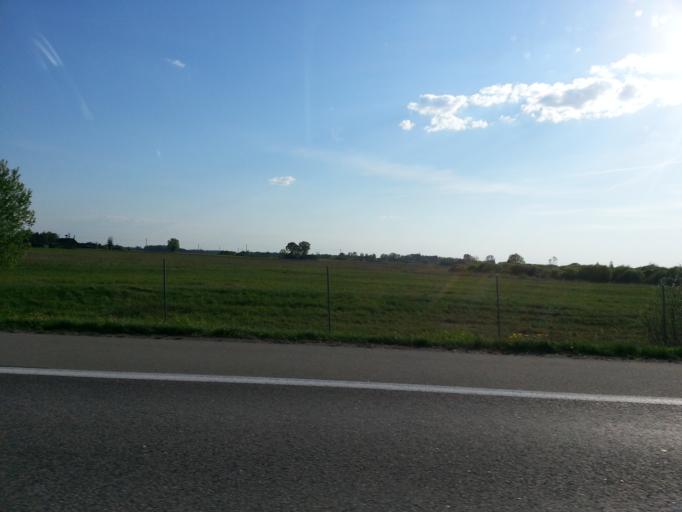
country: LT
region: Vilnius County
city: Ukmerge
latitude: 55.4836
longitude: 24.6366
